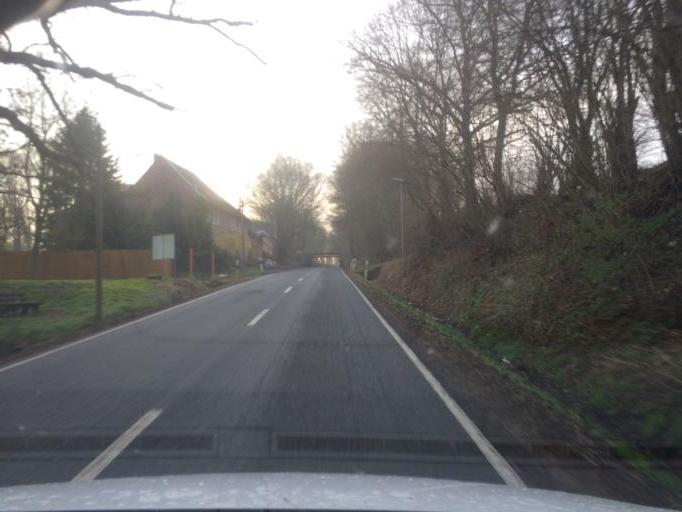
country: DE
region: Thuringia
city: Weissenborn-Luderode
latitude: 51.5282
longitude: 10.4331
